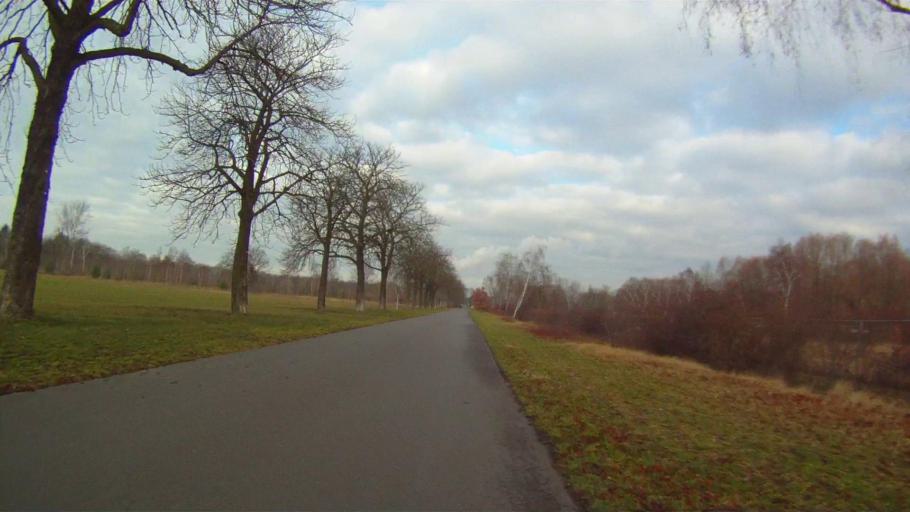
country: DE
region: Berlin
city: Oberschoneweide
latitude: 52.4707
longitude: 13.5253
